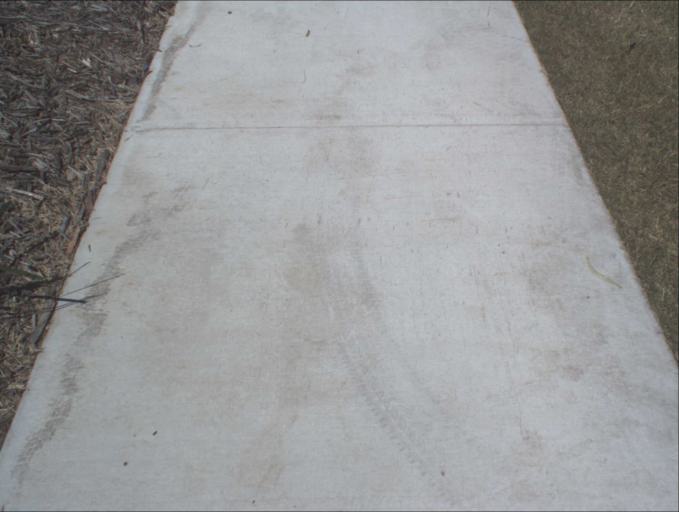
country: AU
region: Queensland
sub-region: Logan
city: North Maclean
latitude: -27.8096
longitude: 152.9559
